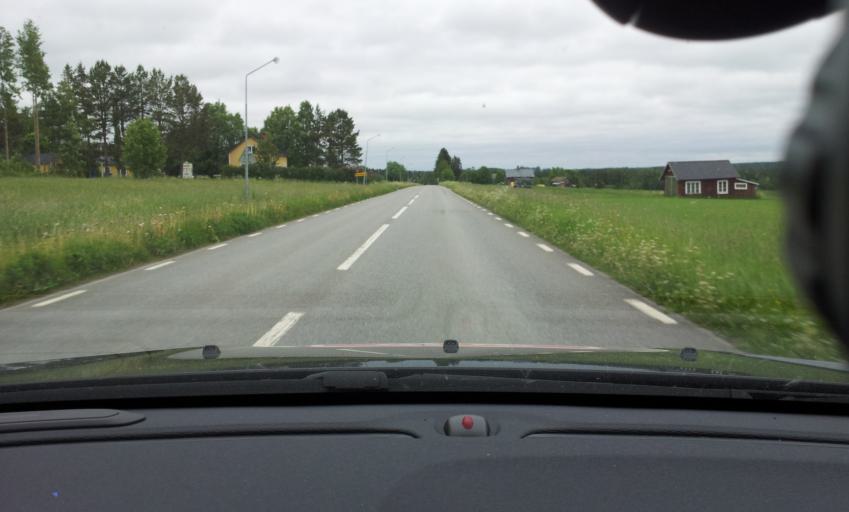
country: SE
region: Jaemtland
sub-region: Bergs Kommun
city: Hoverberg
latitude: 63.0166
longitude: 14.3439
